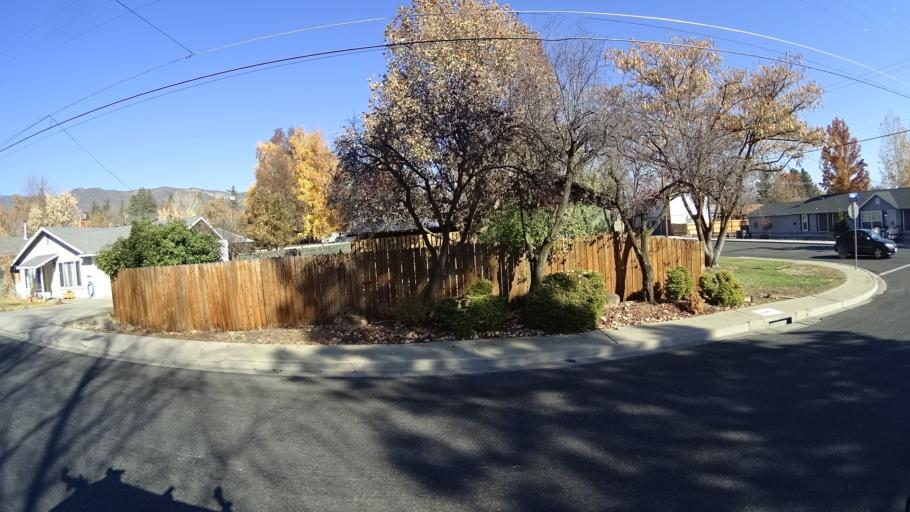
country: US
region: California
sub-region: Siskiyou County
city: Yreka
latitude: 41.7338
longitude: -122.6462
